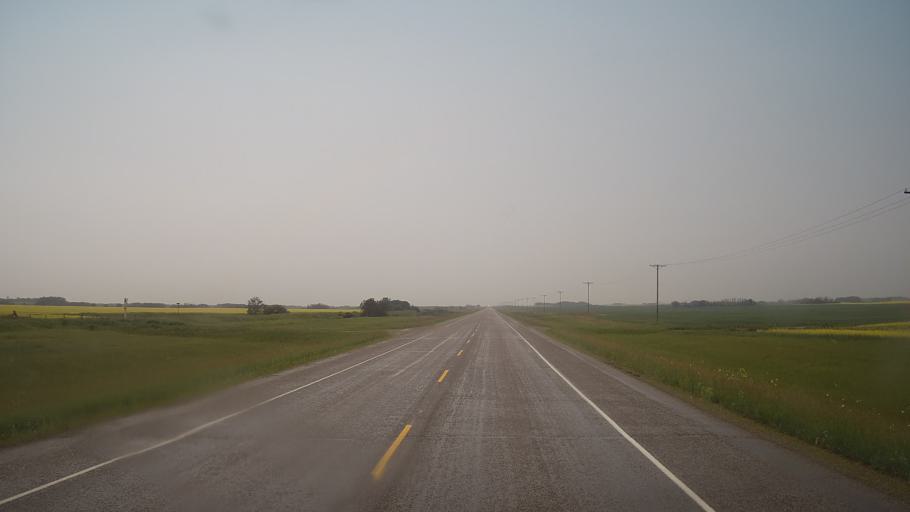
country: CA
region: Saskatchewan
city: Biggar
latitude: 52.1523
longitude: -108.2394
